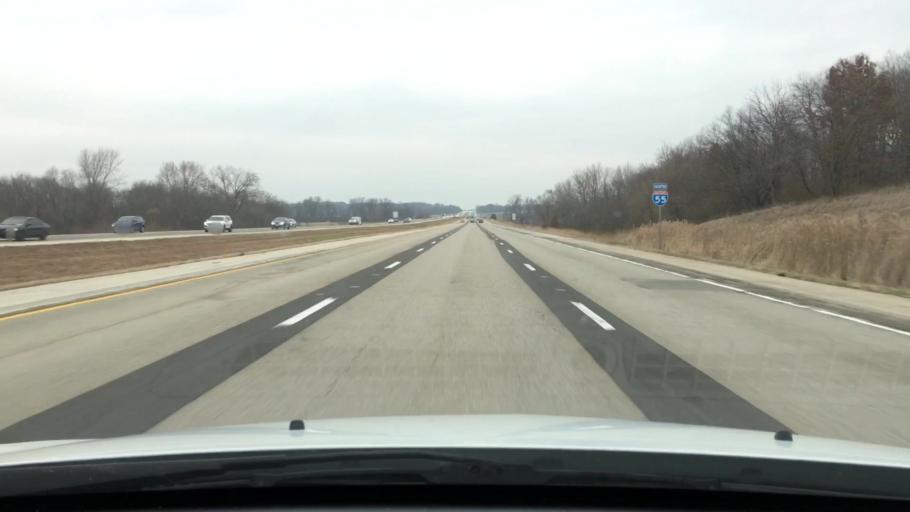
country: US
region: Illinois
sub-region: Logan County
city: Lincoln
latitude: 40.1194
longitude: -89.4164
